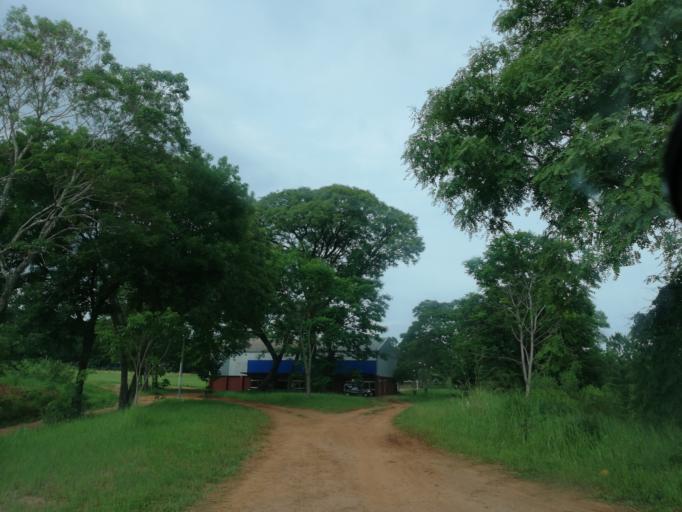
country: AR
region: Misiones
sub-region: Departamento de Capital
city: Posadas
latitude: -27.4364
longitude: -55.8896
